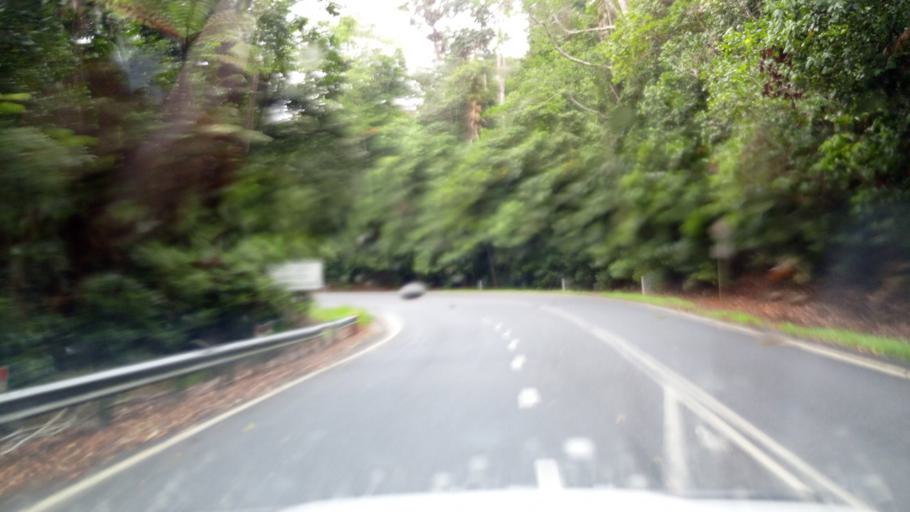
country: AU
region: Queensland
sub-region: Tablelands
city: Tolga
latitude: -17.2199
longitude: 145.6954
